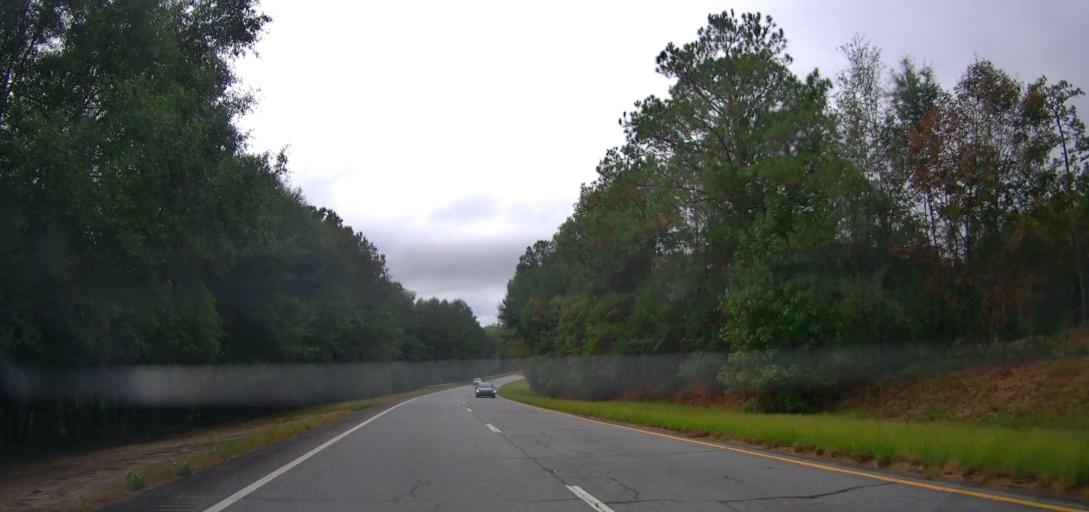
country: US
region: Georgia
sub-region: Thomas County
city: Thomasville
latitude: 30.7736
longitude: -84.0697
